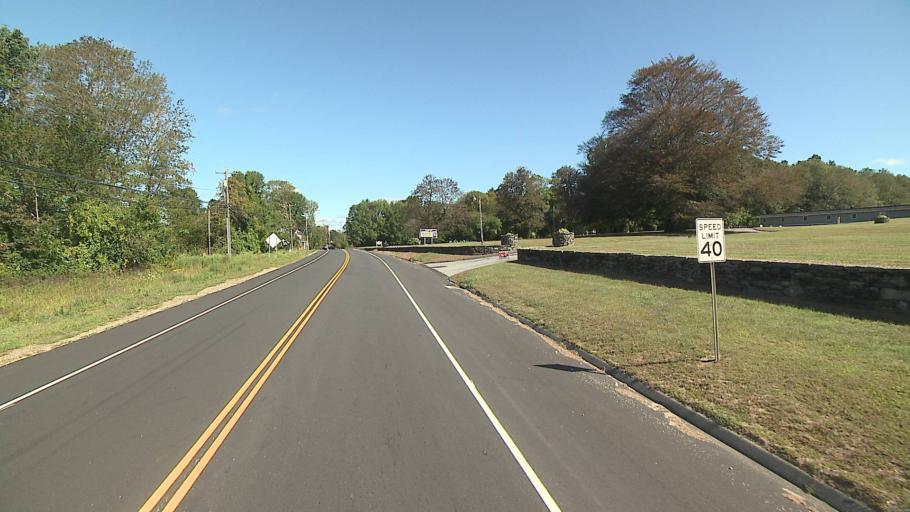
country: US
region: Connecticut
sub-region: Windham County
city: Wauregan
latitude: 41.7446
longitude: -71.9067
